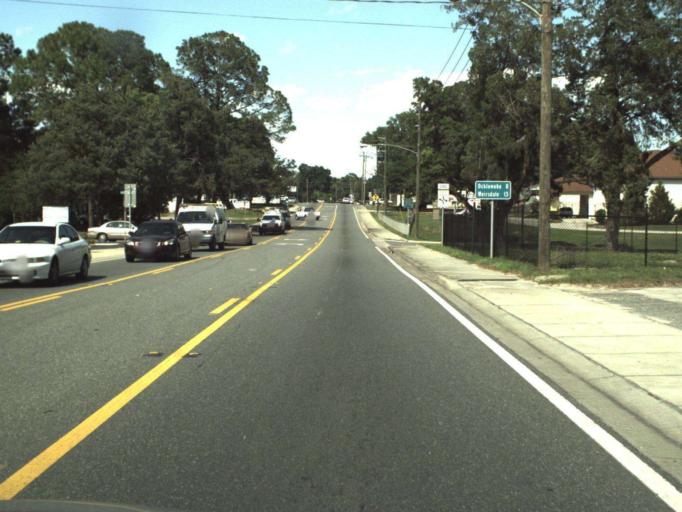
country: US
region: Florida
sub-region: Marion County
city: Belleview
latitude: 29.0600
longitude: -82.0514
